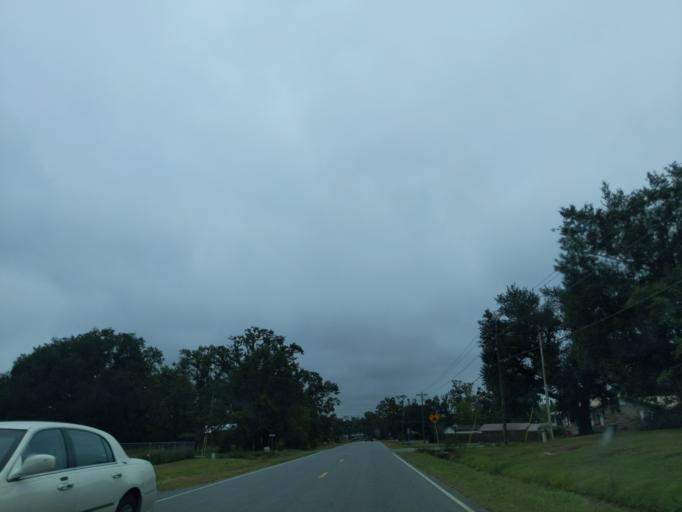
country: US
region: Florida
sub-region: Jackson County
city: Sneads
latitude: 30.7122
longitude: -84.9324
